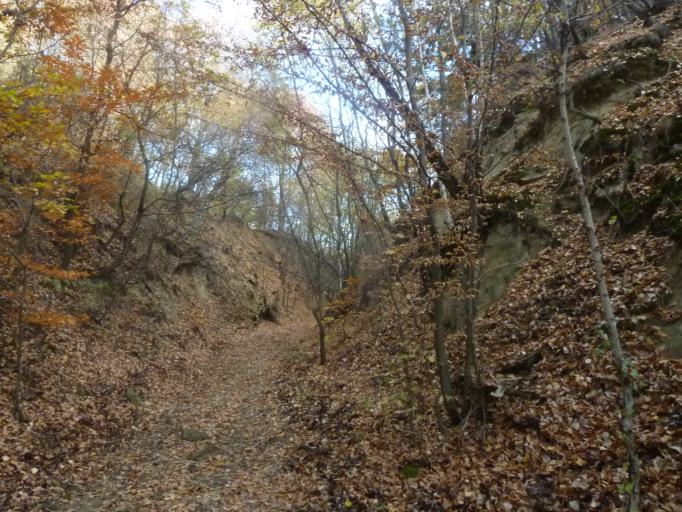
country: HU
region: Nograd
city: Somoskoujfalu
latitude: 48.1314
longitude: 19.8444
